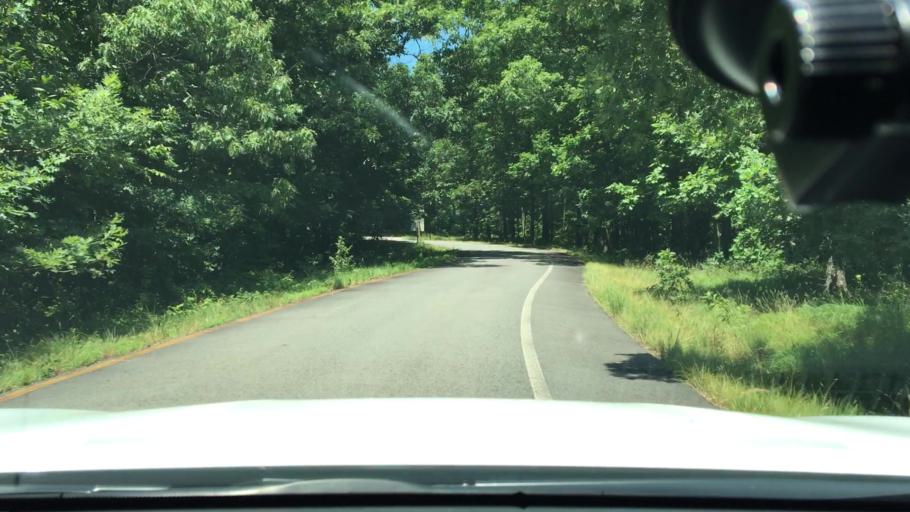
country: US
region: Arkansas
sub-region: Logan County
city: Paris
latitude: 35.1696
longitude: -93.6404
